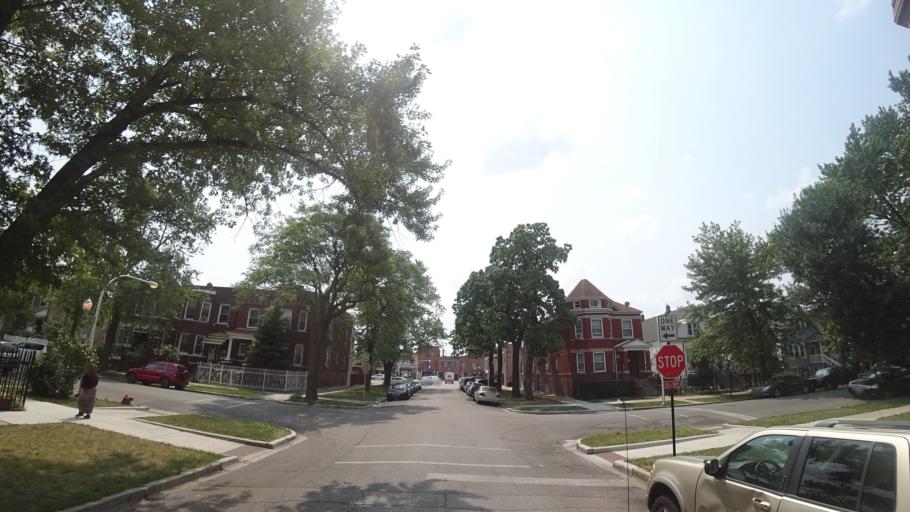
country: US
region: Illinois
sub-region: Cook County
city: Cicero
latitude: 41.8454
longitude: -87.7262
